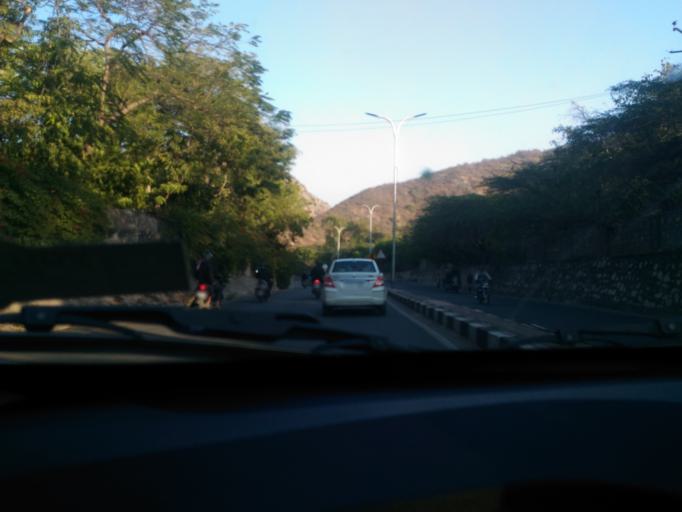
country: IN
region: Rajasthan
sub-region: Jaipur
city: Jaipur
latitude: 26.9017
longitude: 75.8473
